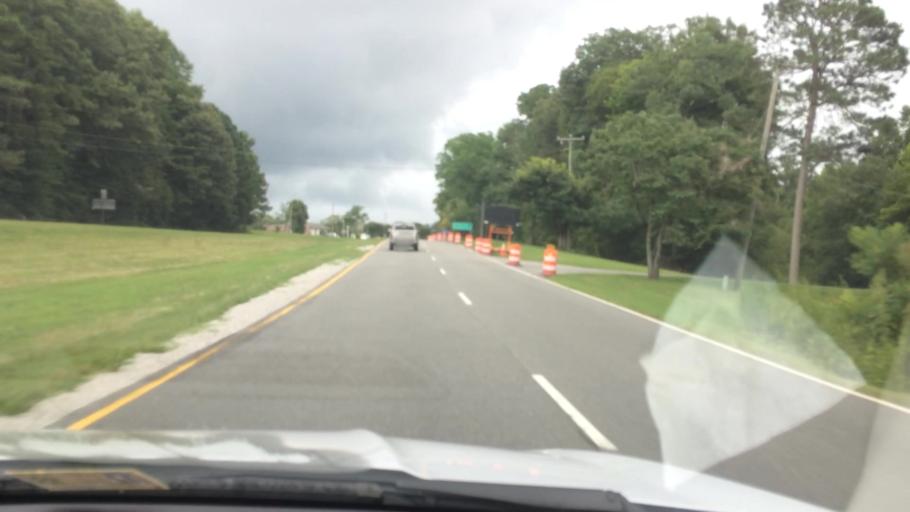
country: US
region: Virginia
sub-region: King William County
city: West Point
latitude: 37.4022
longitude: -76.8130
